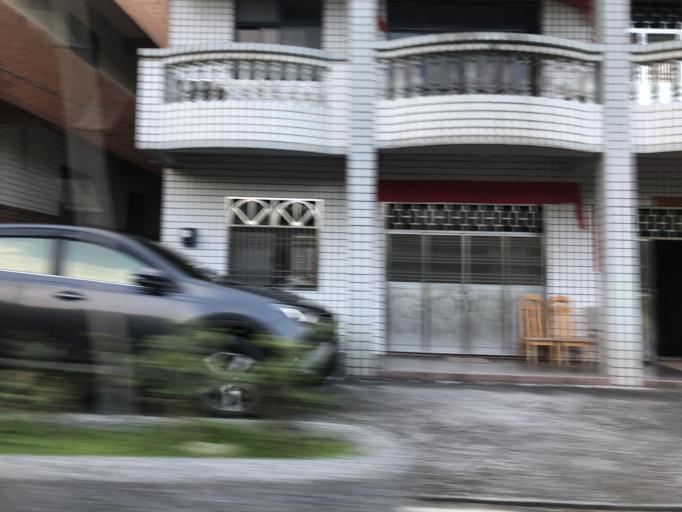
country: TW
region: Taiwan
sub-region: Keelung
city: Keelung
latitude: 25.1994
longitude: 121.6466
